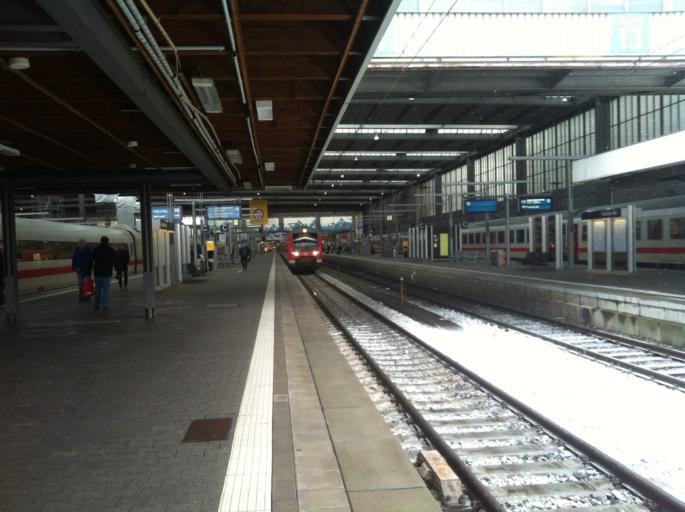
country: DE
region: Bavaria
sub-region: Upper Bavaria
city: Munich
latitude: 48.1402
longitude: 11.5560
